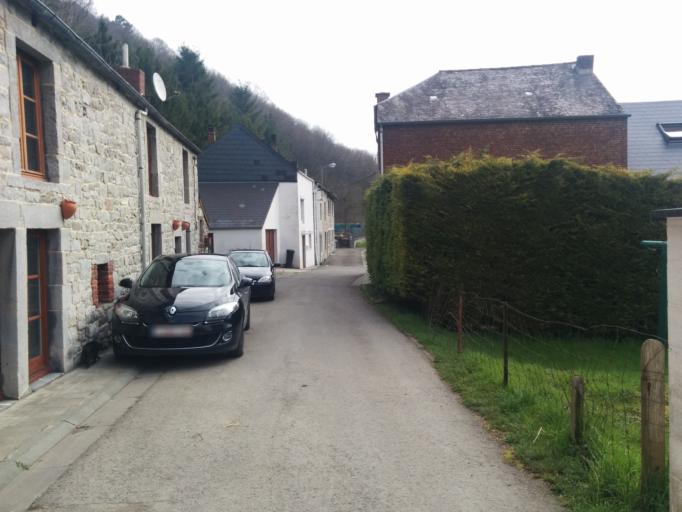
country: FR
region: Champagne-Ardenne
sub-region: Departement des Ardennes
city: Vireux-Molhain
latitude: 50.0940
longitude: 4.6671
